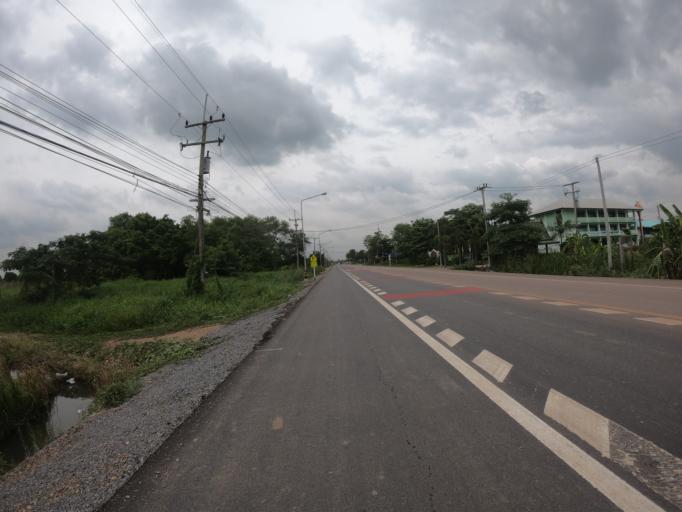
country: TH
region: Pathum Thani
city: Nong Suea
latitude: 14.0373
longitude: 100.8701
